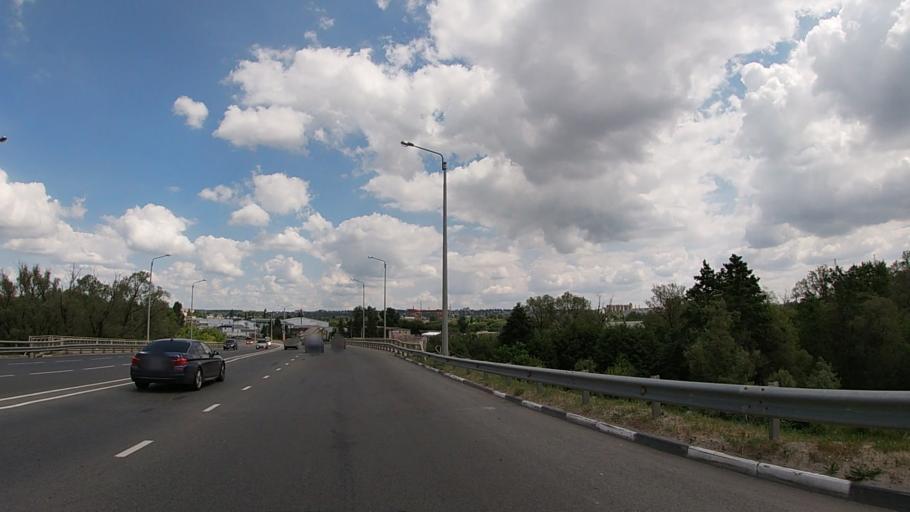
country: RU
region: Belgorod
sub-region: Belgorodskiy Rayon
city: Belgorod
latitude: 50.6073
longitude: 36.5323
